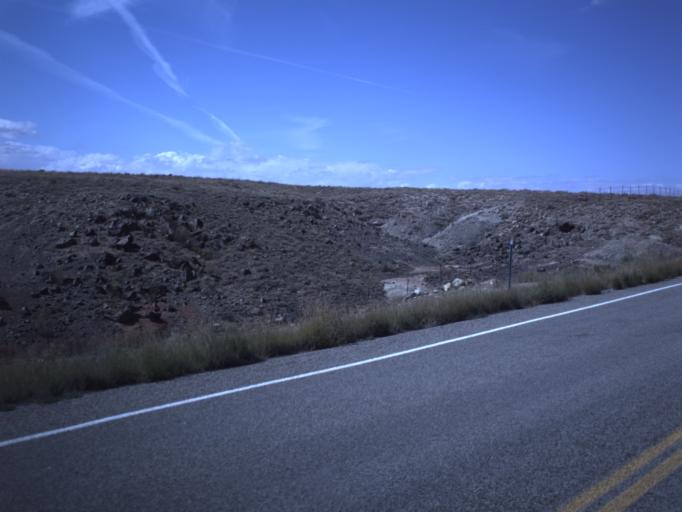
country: US
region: Colorado
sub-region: Montezuma County
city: Towaoc
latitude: 37.1751
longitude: -109.1035
